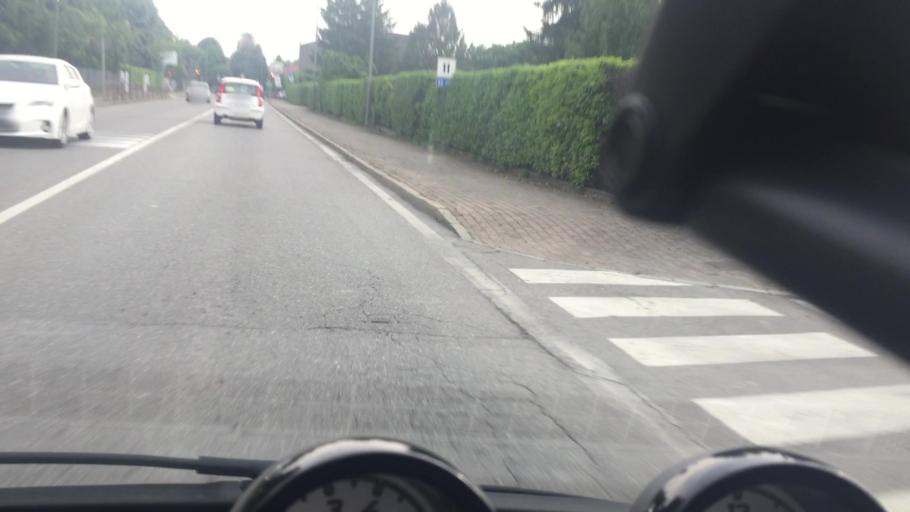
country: IT
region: Lombardy
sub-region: Provincia di Bergamo
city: Boltiere
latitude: 45.6039
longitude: 9.5812
